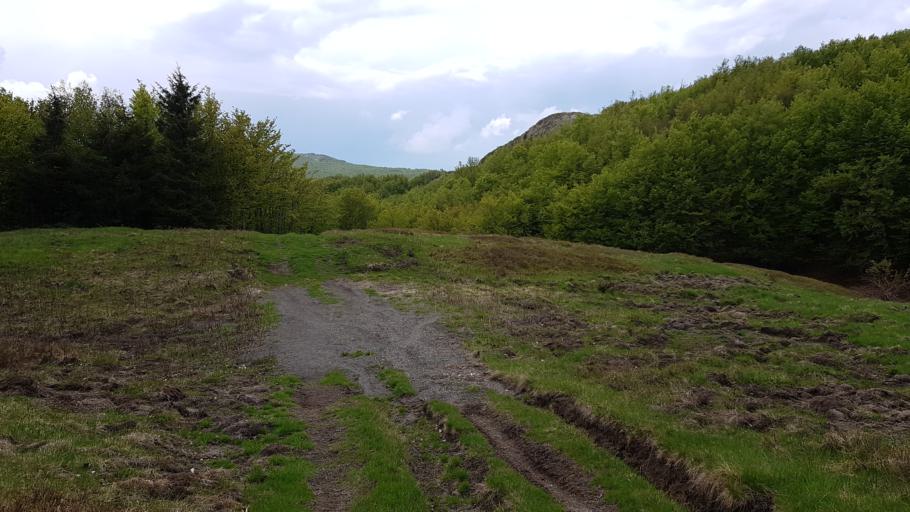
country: IT
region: Liguria
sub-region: Provincia di Genova
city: Santo Stefano d'Aveto
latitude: 44.5594
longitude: 9.4895
